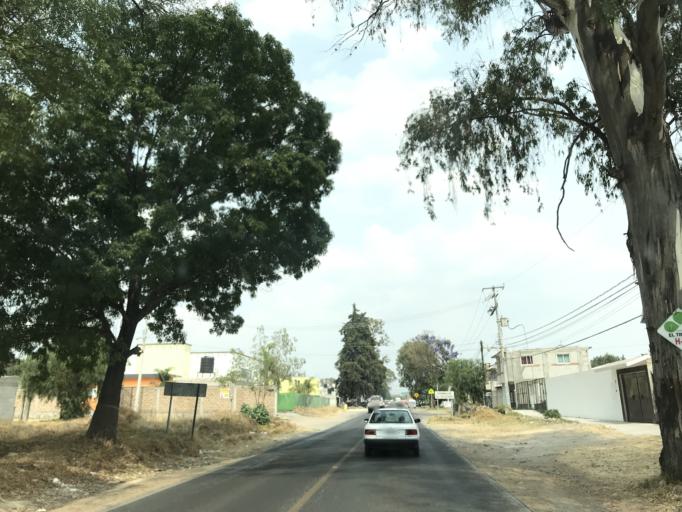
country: MX
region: Tlaxcala
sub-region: Panotla
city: Fraccionamiento la Virgen
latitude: 19.3195
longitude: -98.2760
